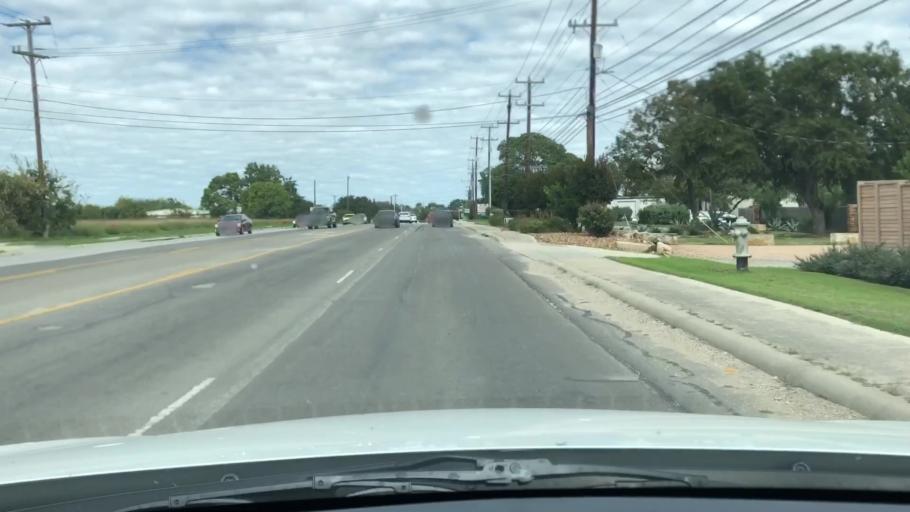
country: US
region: Texas
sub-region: Bexar County
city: Leon Valley
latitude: 29.4920
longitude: -98.6209
